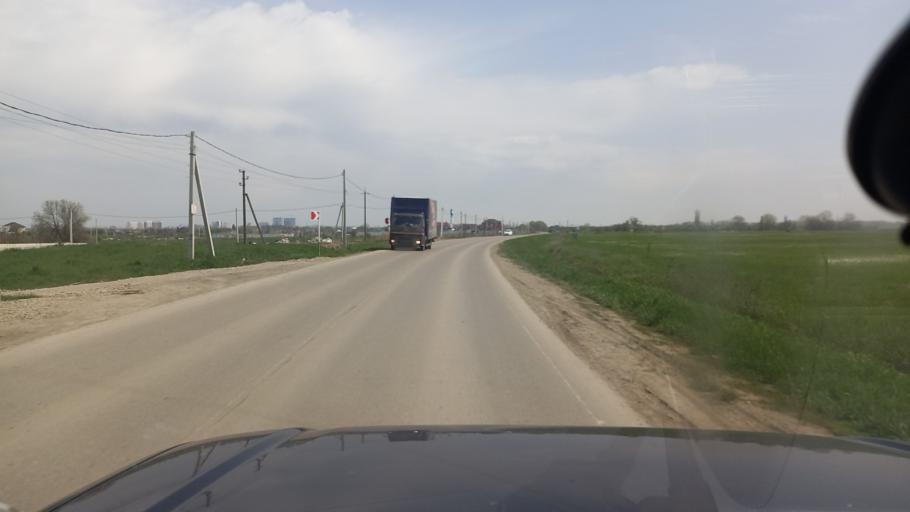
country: RU
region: Adygeya
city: Yablonovskiy
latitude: 44.9868
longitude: 38.9821
